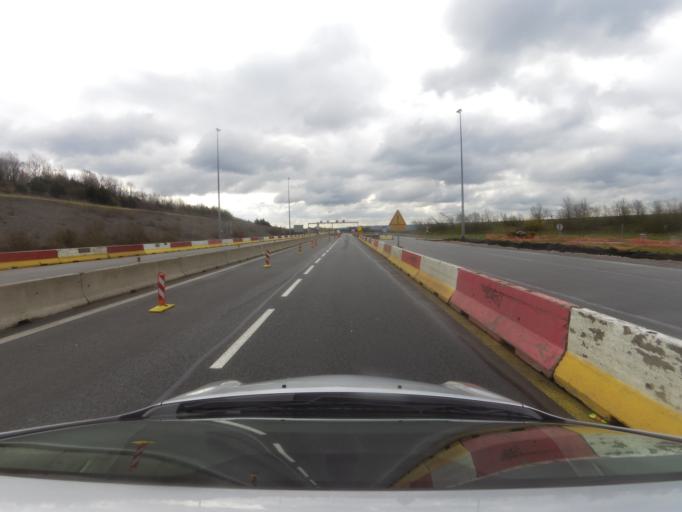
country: FR
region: Nord-Pas-de-Calais
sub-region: Departement du Pas-de-Calais
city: Saint-Etienne-au-Mont
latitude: 50.6876
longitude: 1.6430
